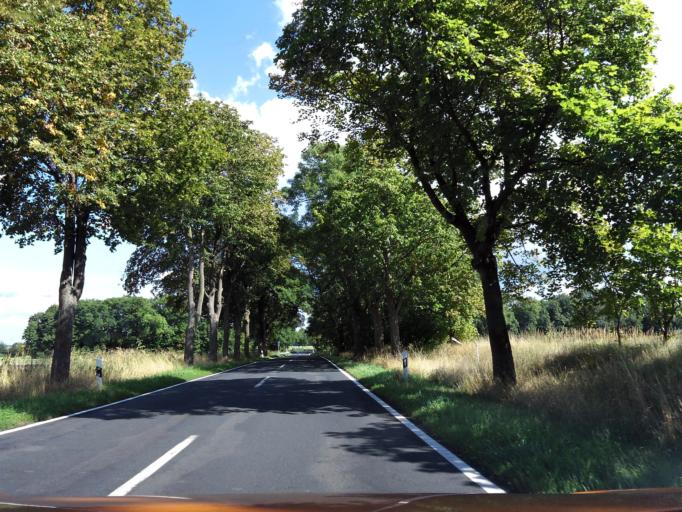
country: DE
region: Brandenburg
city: Ketzin
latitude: 52.4646
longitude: 12.8988
